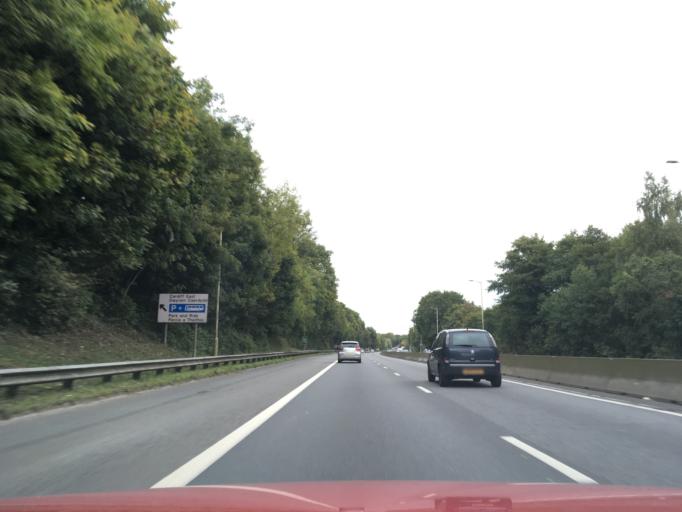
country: GB
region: Wales
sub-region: Cardiff
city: Cardiff
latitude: 51.5146
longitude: -3.1435
